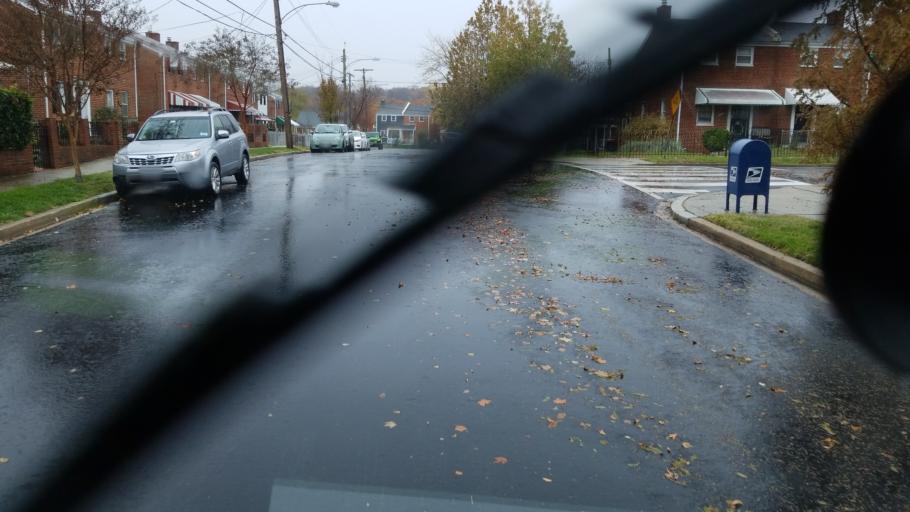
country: US
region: Maryland
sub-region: Prince George's County
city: Coral Hills
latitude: 38.8813
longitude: -76.9406
